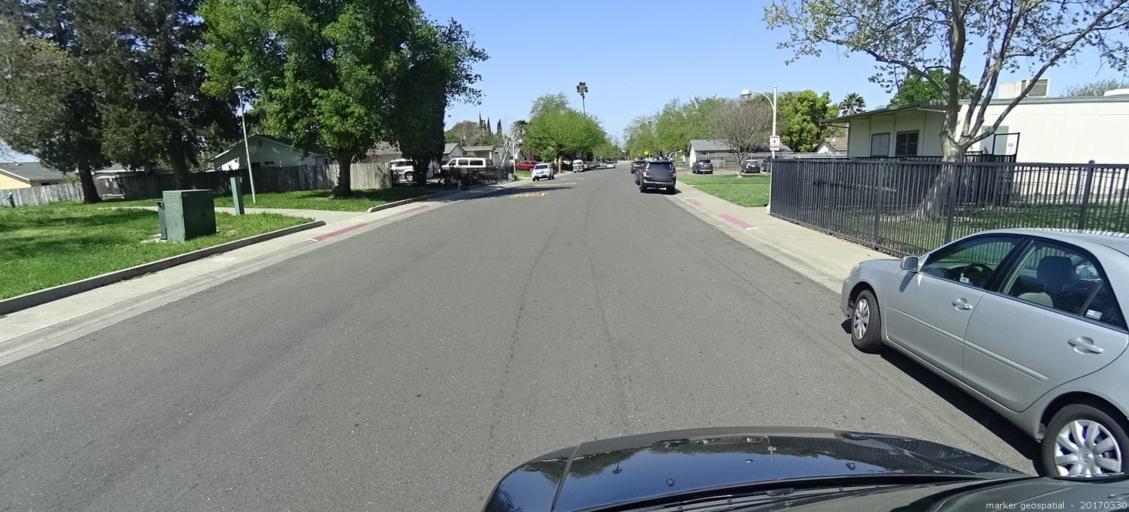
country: US
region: California
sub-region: Sacramento County
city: Florin
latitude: 38.4630
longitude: -121.4237
